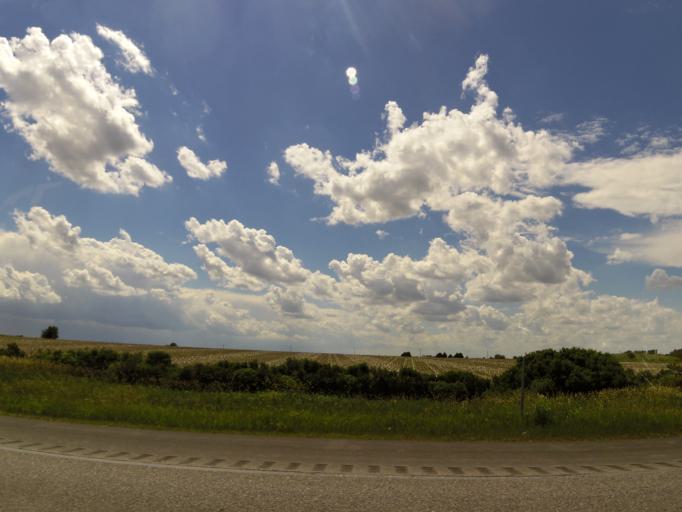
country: US
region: Iowa
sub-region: Linn County
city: Ely
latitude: 41.8608
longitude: -91.6690
